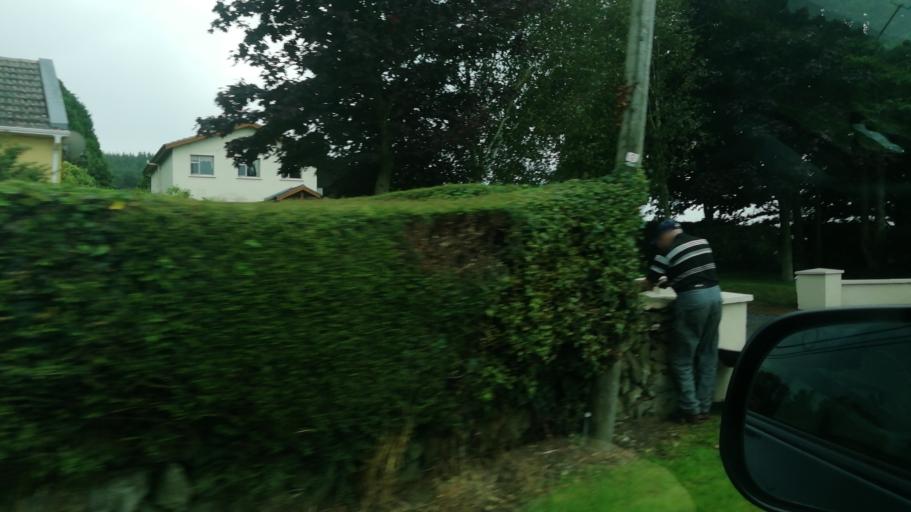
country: IE
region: Munster
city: Fethard
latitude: 52.4838
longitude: -7.6934
